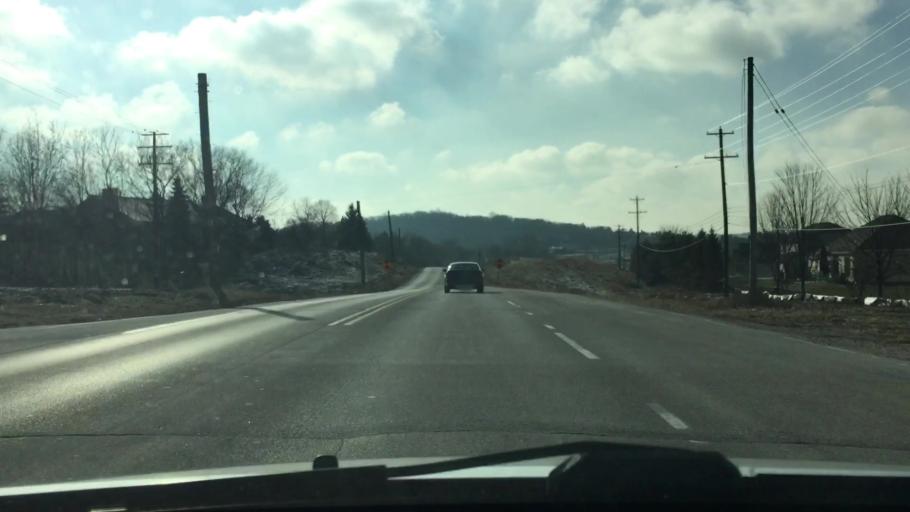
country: US
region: Wisconsin
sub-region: Waukesha County
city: Waukesha
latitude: 43.0154
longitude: -88.2860
